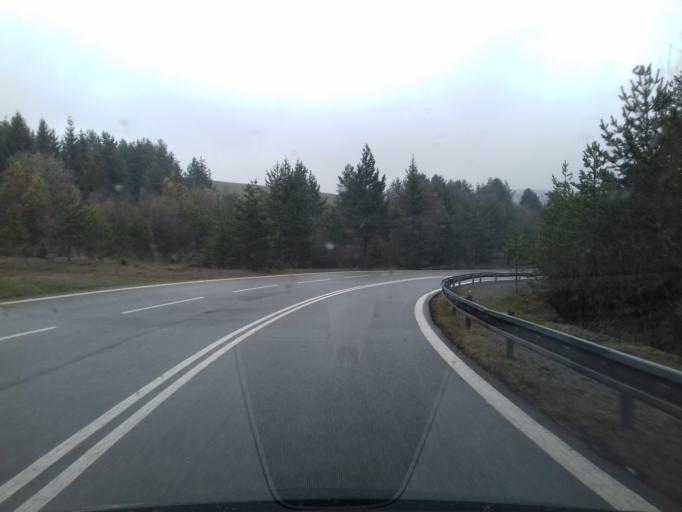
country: SK
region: Presovsky
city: Stara L'ubovna
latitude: 49.3537
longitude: 20.6772
